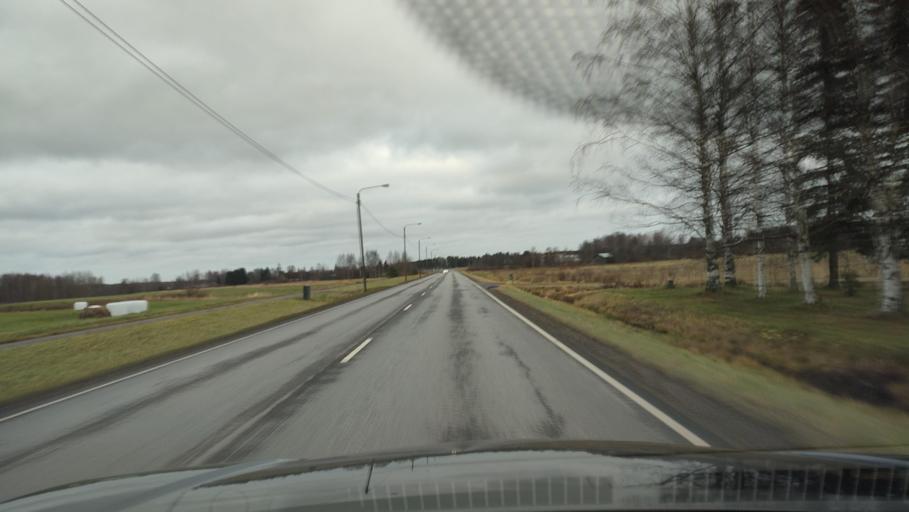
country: FI
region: Southern Ostrobothnia
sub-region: Seinaejoki
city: Kurikka
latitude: 62.6081
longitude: 22.4201
